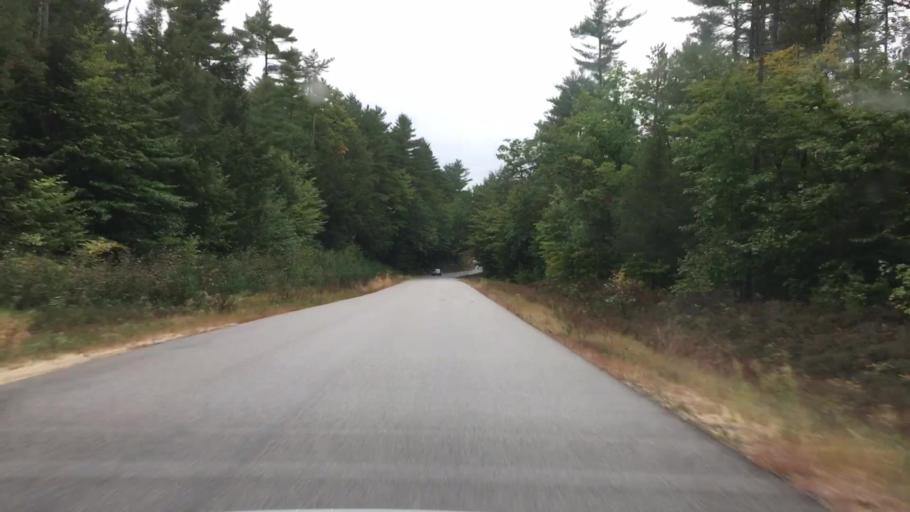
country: US
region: Maine
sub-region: Cumberland County
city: Harrison
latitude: 44.0297
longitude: -70.5964
